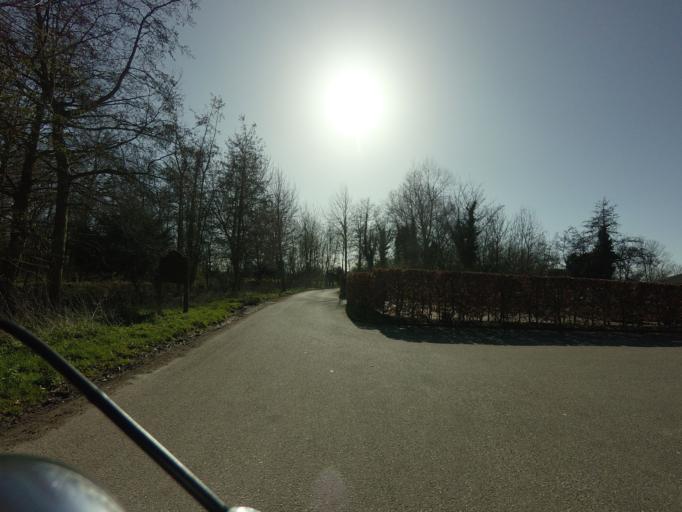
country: NL
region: Zeeland
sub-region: Schouwen-Duiveland
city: Renesse
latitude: 51.7327
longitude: 3.7835
